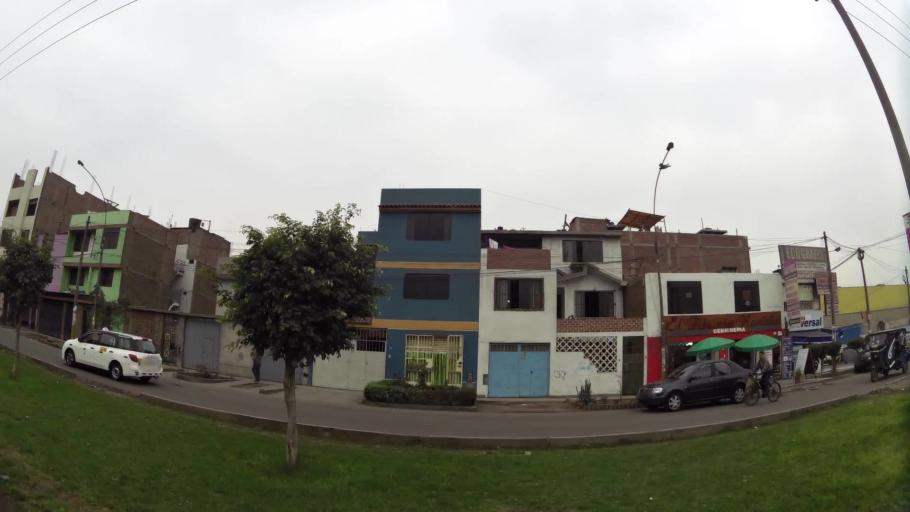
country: PE
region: Lima
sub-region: Lima
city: Independencia
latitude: -11.9745
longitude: -77.0021
